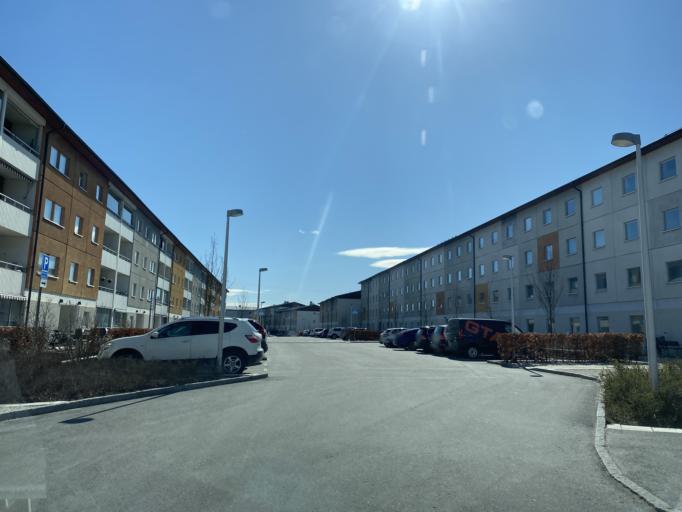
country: SE
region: Stockholm
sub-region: Stockholms Kommun
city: Arsta
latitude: 59.2846
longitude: 18.0377
